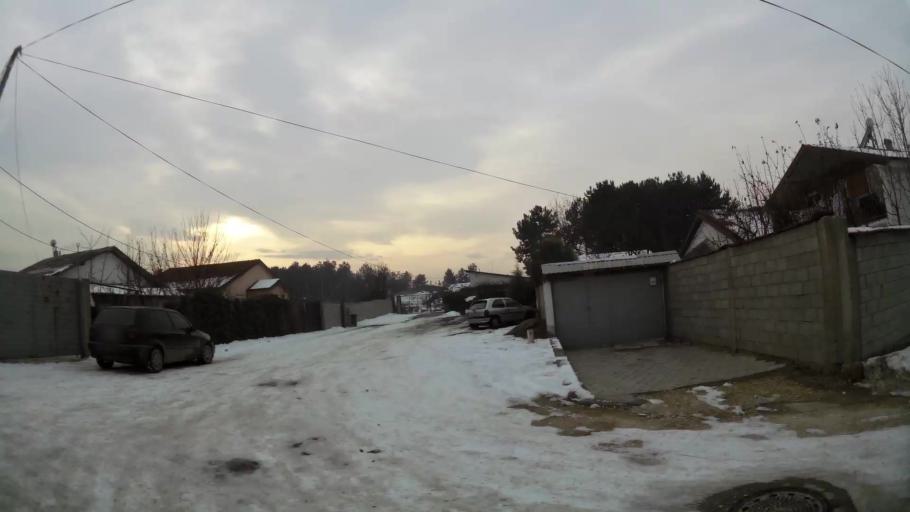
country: MK
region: Suto Orizari
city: Suto Orizare
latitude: 42.0420
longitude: 21.4306
